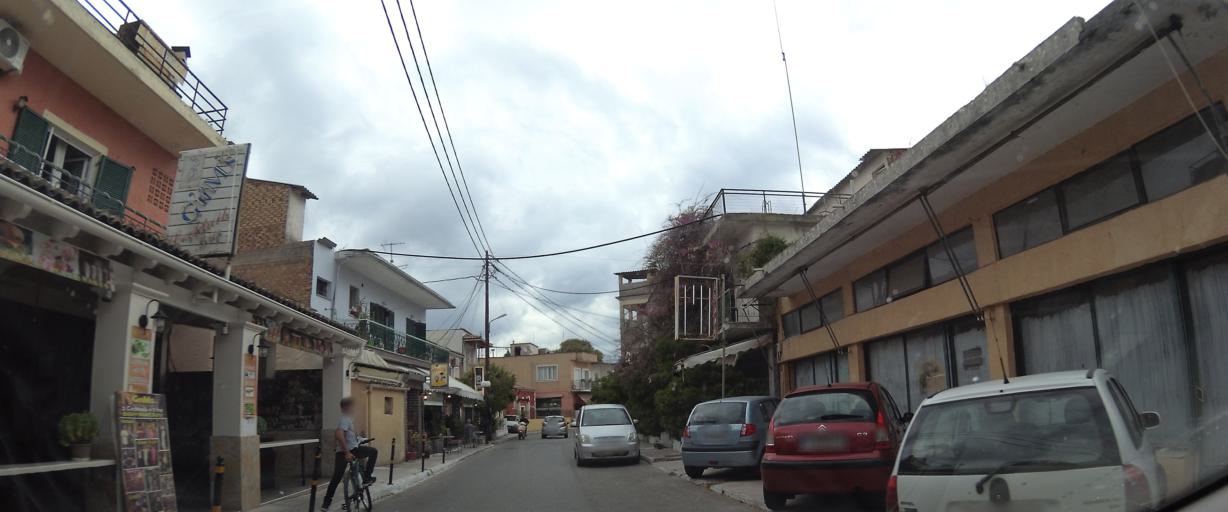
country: GR
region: Ionian Islands
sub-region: Nomos Kerkyras
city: Kontokali
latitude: 39.6451
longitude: 19.8518
